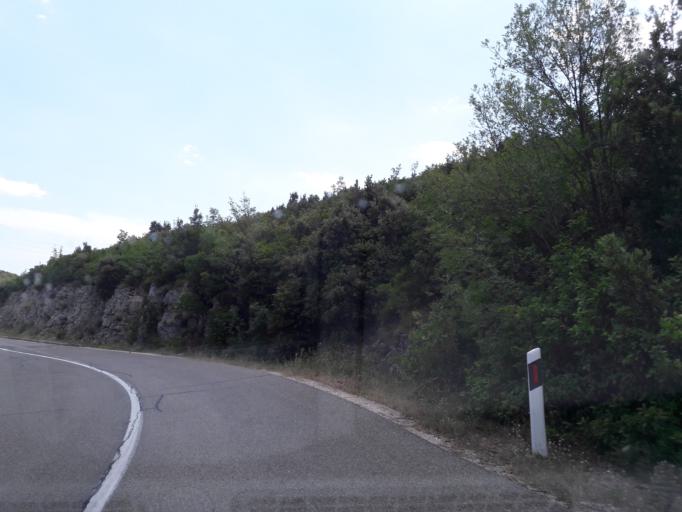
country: HR
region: Dubrovacko-Neretvanska
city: Orebic
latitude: 42.9755
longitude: 17.2669
